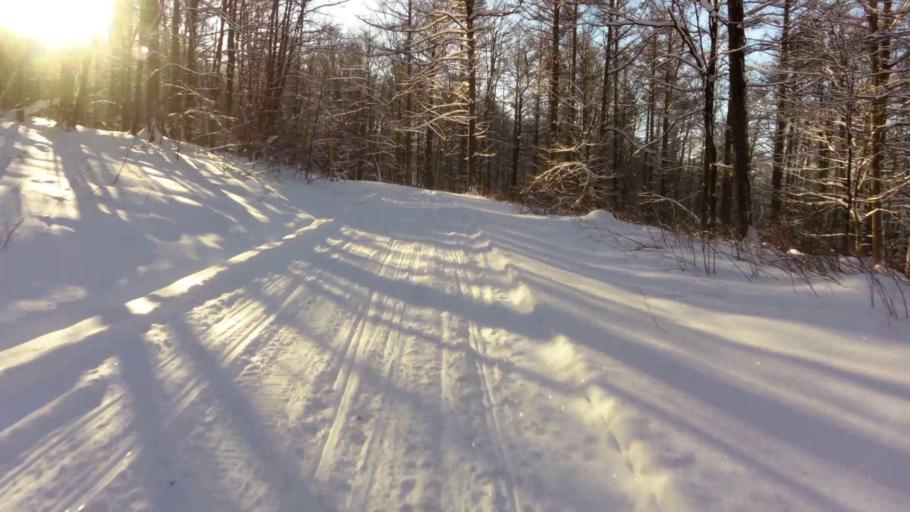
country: US
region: New York
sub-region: Chautauqua County
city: Falconer
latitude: 42.2278
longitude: -79.2301
